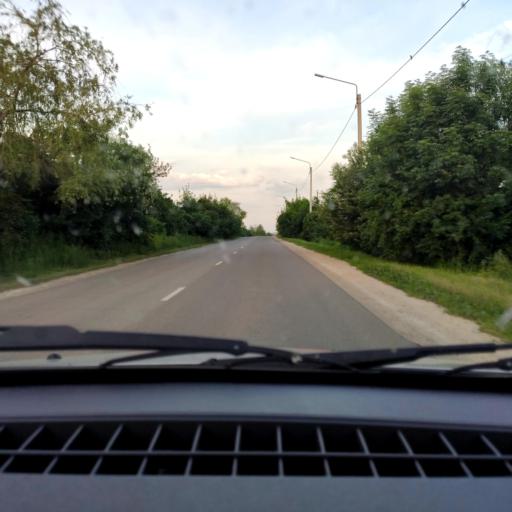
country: RU
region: Voronezj
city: Ramon'
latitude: 51.9522
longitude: 39.3638
